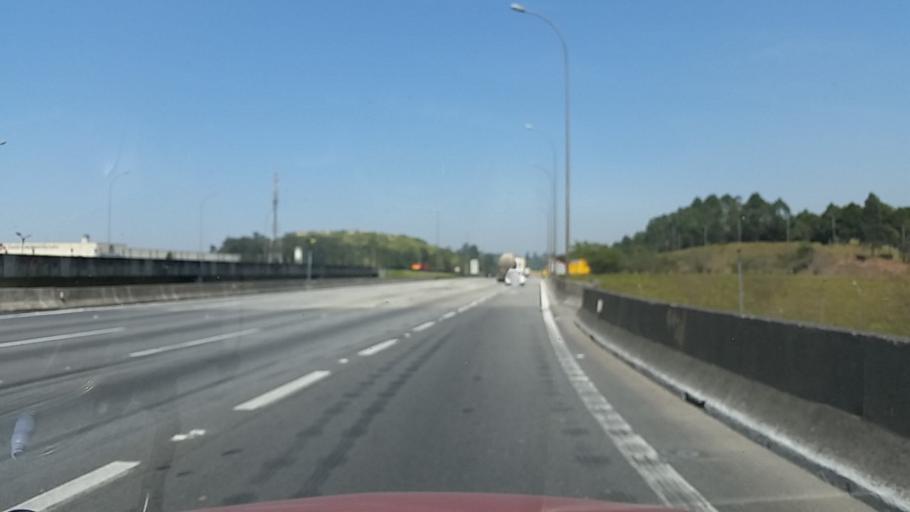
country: BR
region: Sao Paulo
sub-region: Taboao Da Serra
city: Taboao da Serra
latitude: -23.5914
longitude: -46.8103
